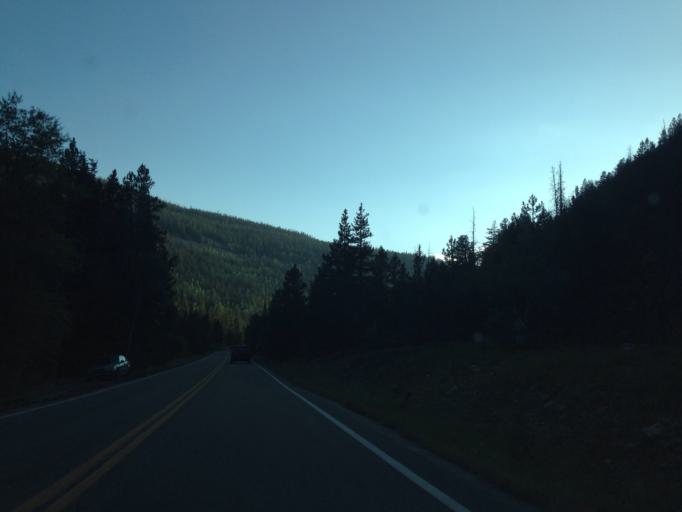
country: US
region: Utah
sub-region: Summit County
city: Francis
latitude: 40.5970
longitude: -110.9736
